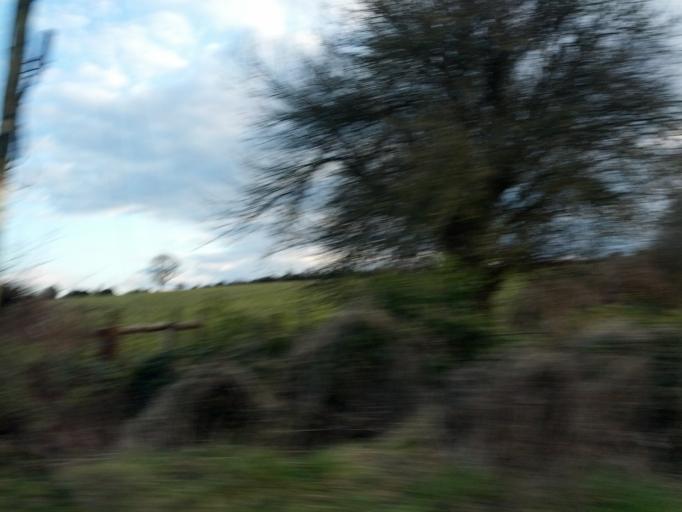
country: IE
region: Connaught
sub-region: County Galway
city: Athenry
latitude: 53.4308
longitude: -8.7011
